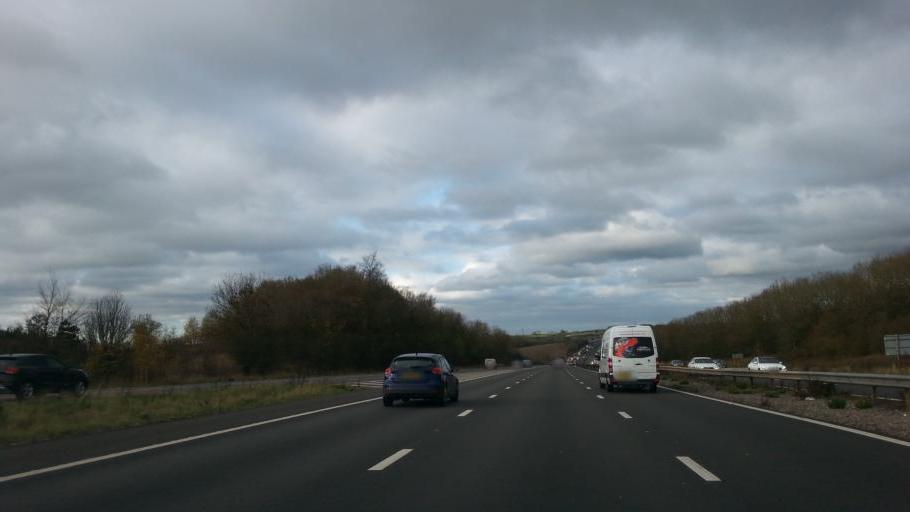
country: GB
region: England
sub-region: Warwickshire
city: Rugby
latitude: 52.4087
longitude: -1.2511
